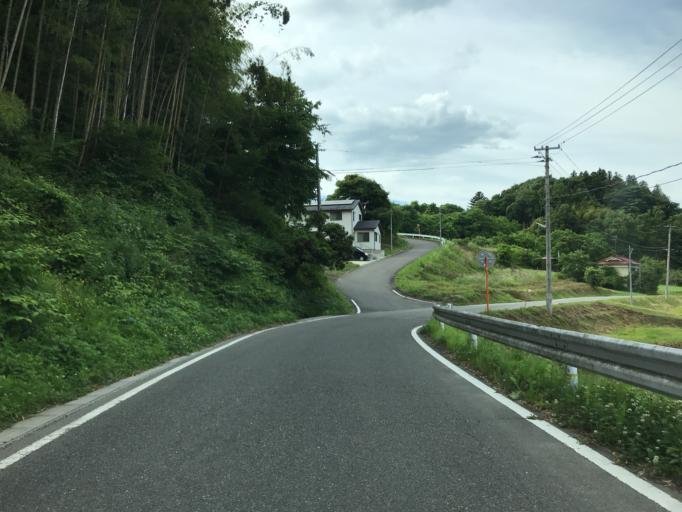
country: JP
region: Fukushima
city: Funehikimachi-funehiki
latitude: 37.4928
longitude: 140.5469
